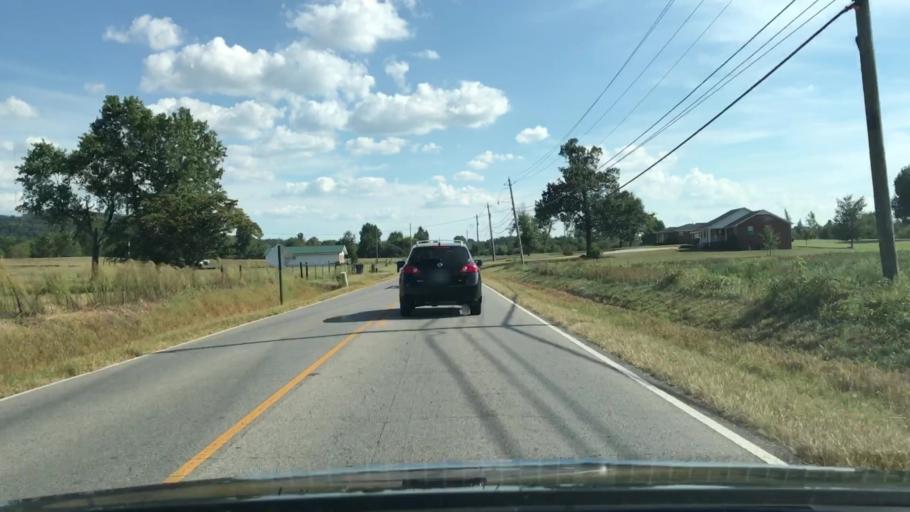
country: US
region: Alabama
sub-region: Madison County
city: Harvest
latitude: 34.8372
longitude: -86.7492
